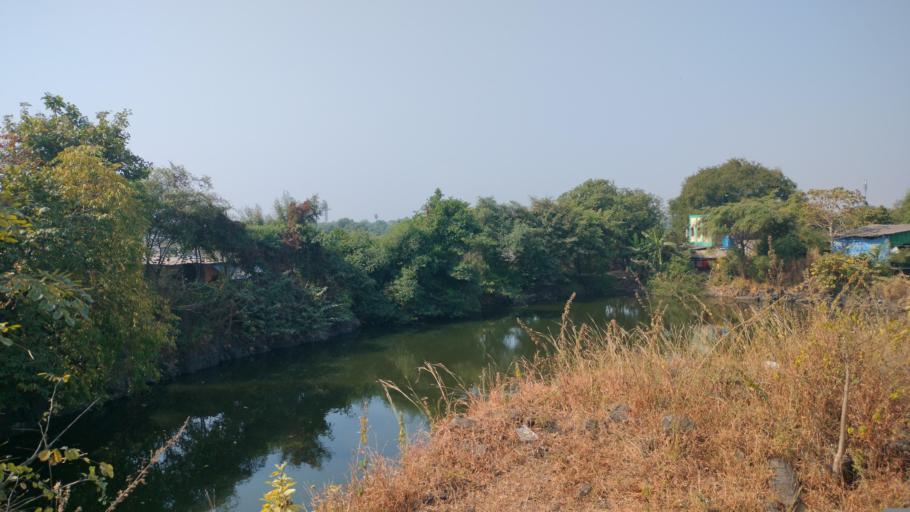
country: IN
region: Maharashtra
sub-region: Thane
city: Virar
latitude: 19.3904
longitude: 72.8649
